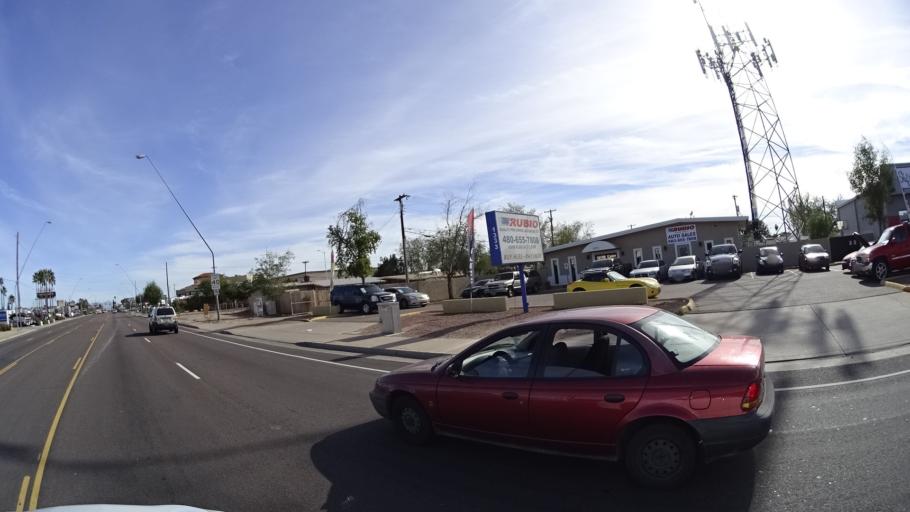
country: US
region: Arizona
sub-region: Maricopa County
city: Mesa
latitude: 33.4076
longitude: -111.8603
